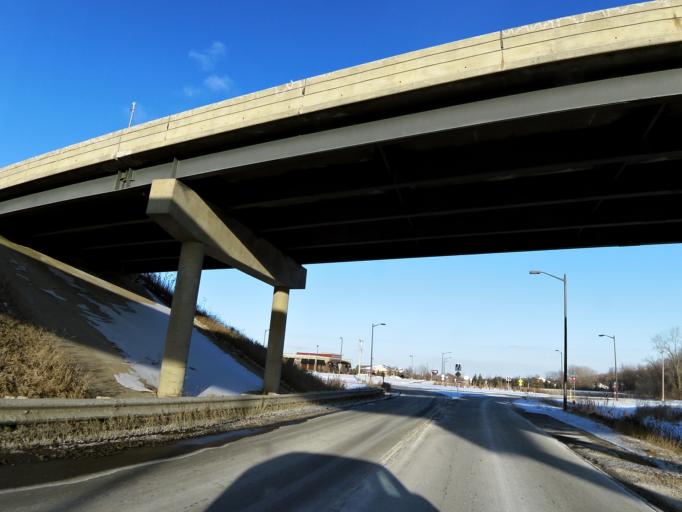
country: US
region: Minnesota
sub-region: Dakota County
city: Lakeville
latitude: 44.6526
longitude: -93.2949
